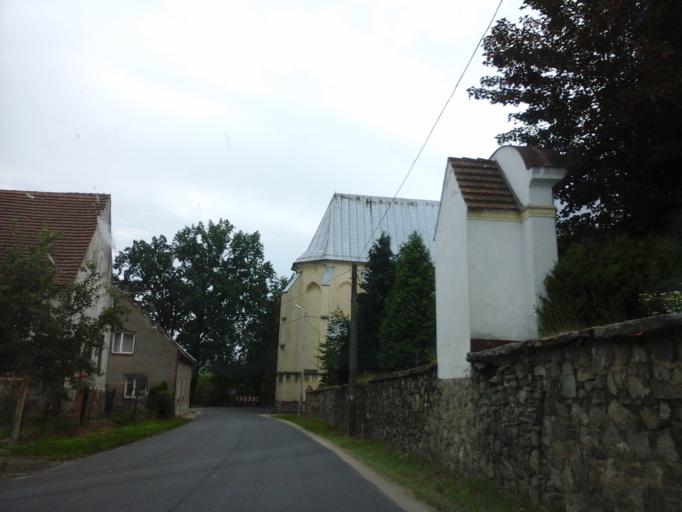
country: PL
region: Lower Silesian Voivodeship
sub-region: Powiat zabkowicki
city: Zabkowice Slaskie
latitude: 50.6235
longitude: 16.8581
